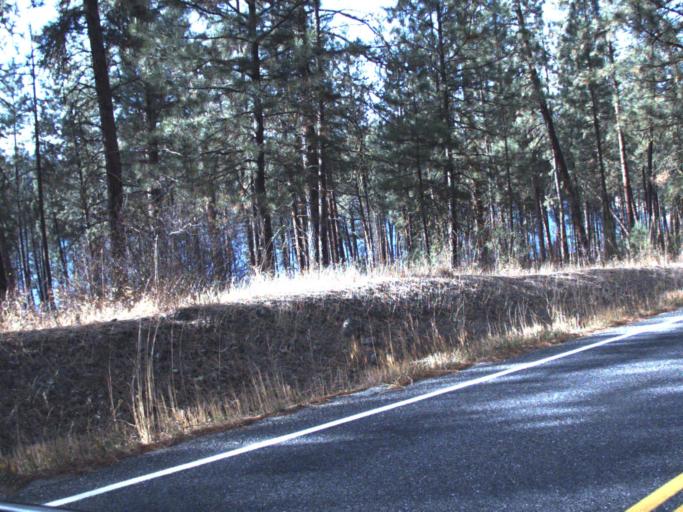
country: US
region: Washington
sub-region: Stevens County
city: Kettle Falls
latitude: 48.2924
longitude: -118.1425
